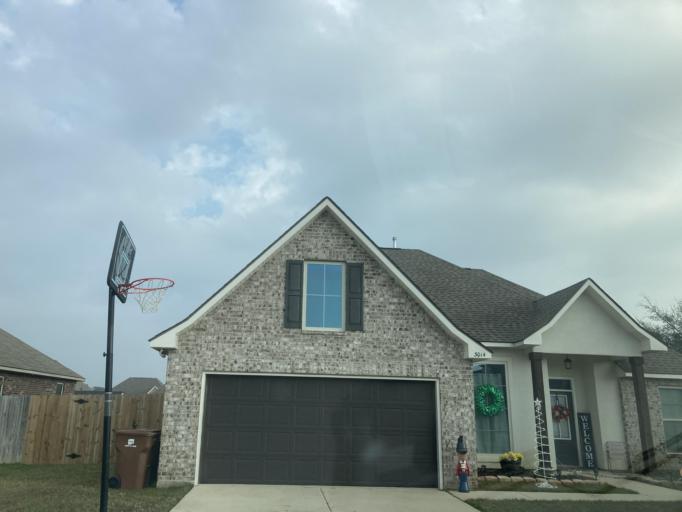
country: US
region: Mississippi
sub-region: Harrison County
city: Long Beach
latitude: 30.3720
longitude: -89.1602
